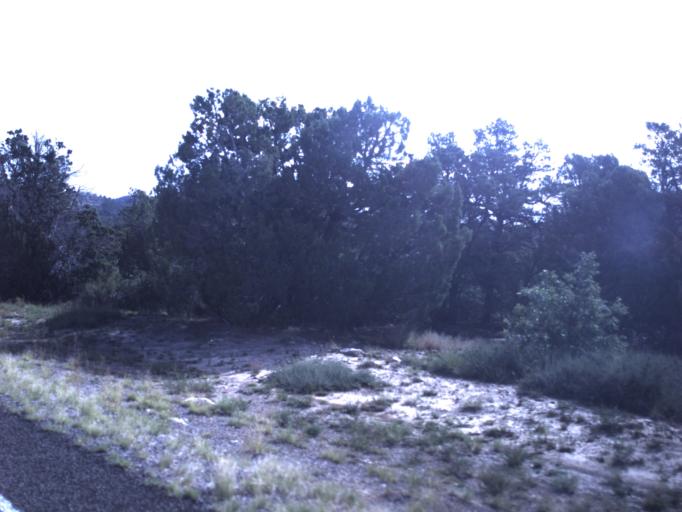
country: US
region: Utah
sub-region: Washington County
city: Hildale
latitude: 37.2560
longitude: -112.7927
